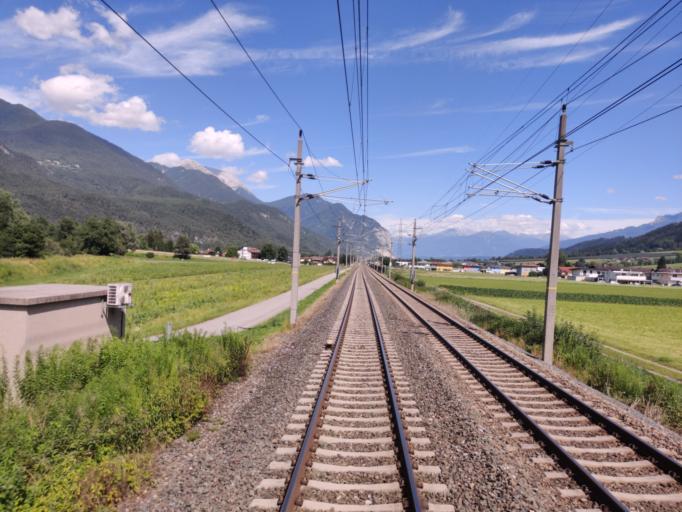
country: AT
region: Tyrol
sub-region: Politischer Bezirk Innsbruck Land
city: Hatting
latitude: 47.2818
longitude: 11.1642
